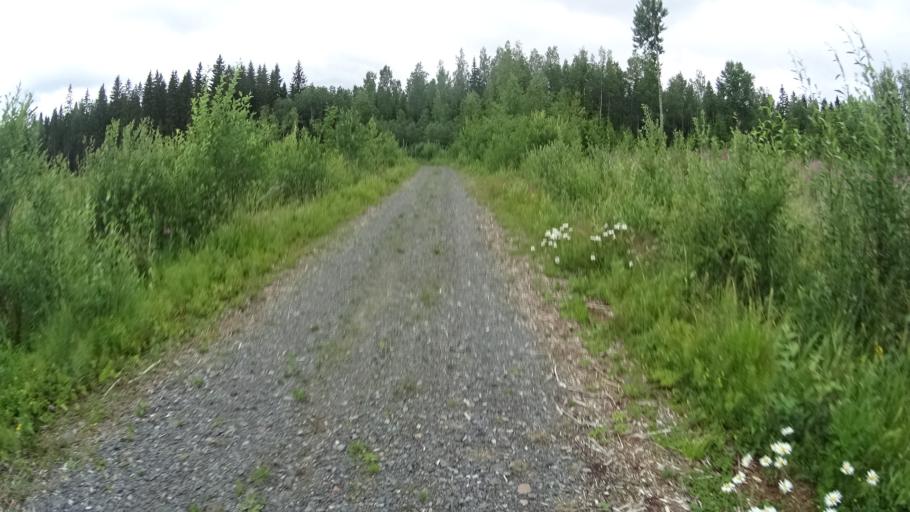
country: FI
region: Uusimaa
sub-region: Helsinki
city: Karkkila
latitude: 60.5663
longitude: 24.3356
